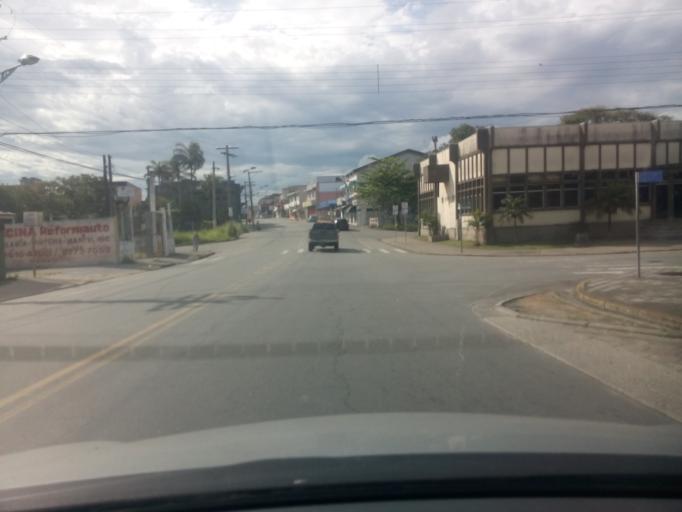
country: BR
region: Sao Paulo
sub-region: Peruibe
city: Peruibe
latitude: -24.3213
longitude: -47.0031
